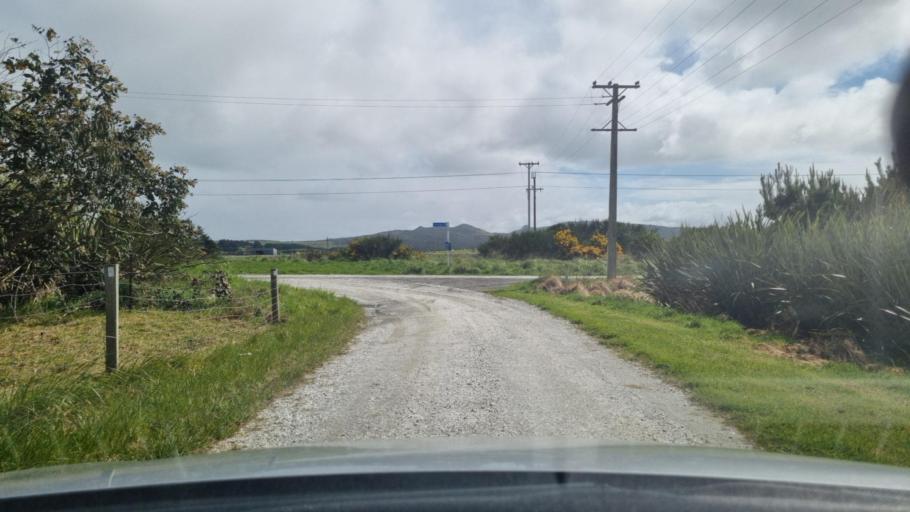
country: NZ
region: Southland
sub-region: Invercargill City
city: Bluff
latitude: -46.5438
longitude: 168.3025
